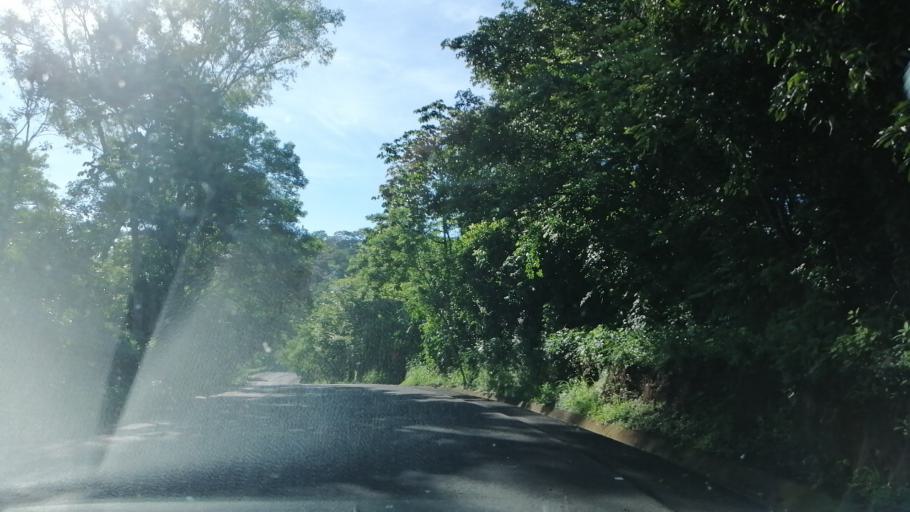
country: SV
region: Morazan
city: Cacaopera
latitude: 13.7900
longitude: -88.1285
